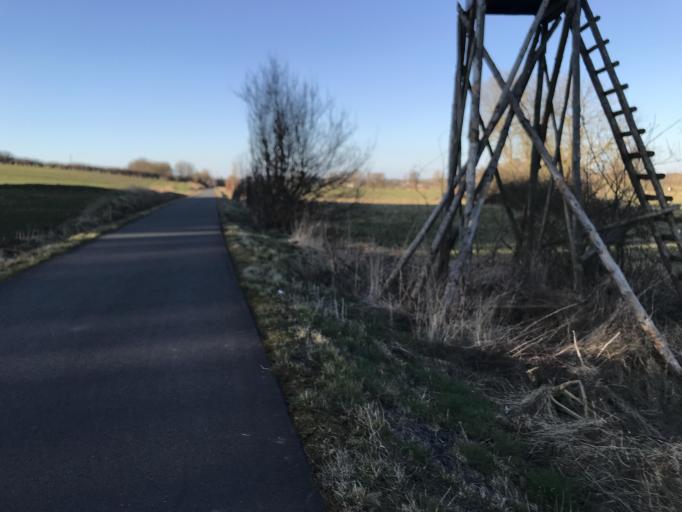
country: DE
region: Hesse
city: Schwalmstadt
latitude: 50.8940
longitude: 9.2412
